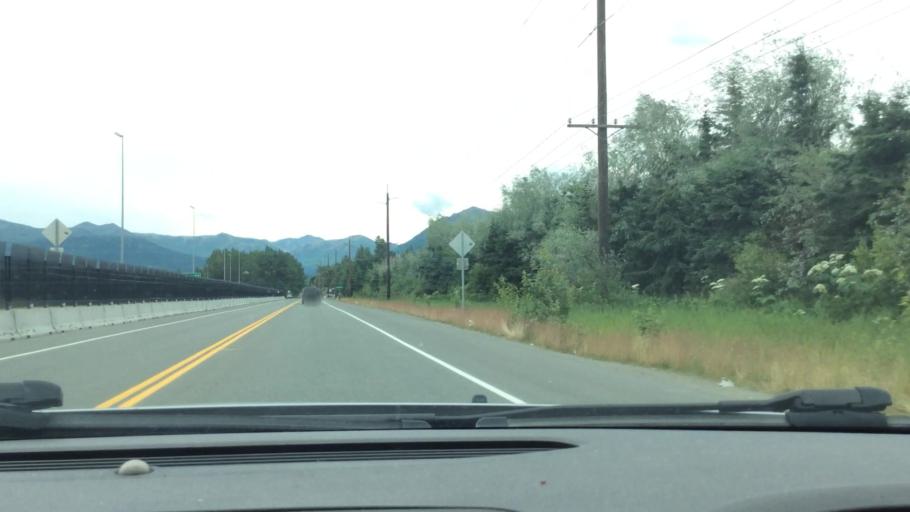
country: US
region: Alaska
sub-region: Anchorage Municipality
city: Elmendorf Air Force Base
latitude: 61.2243
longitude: -149.7525
